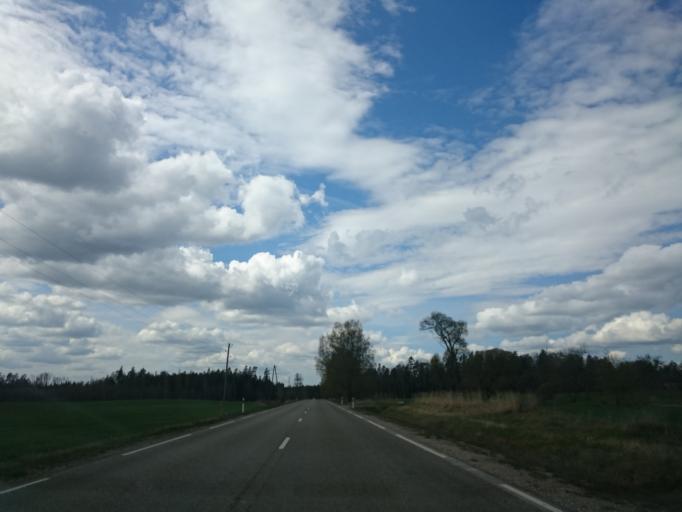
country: LV
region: Talsu Rajons
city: Sabile
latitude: 56.9519
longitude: 22.3070
